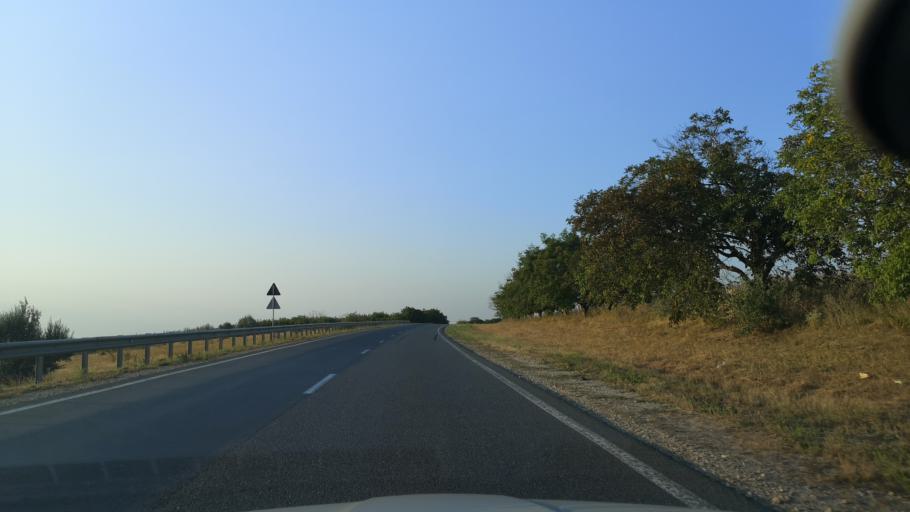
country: MD
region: Rezina
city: Saharna
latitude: 47.6064
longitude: 28.8307
